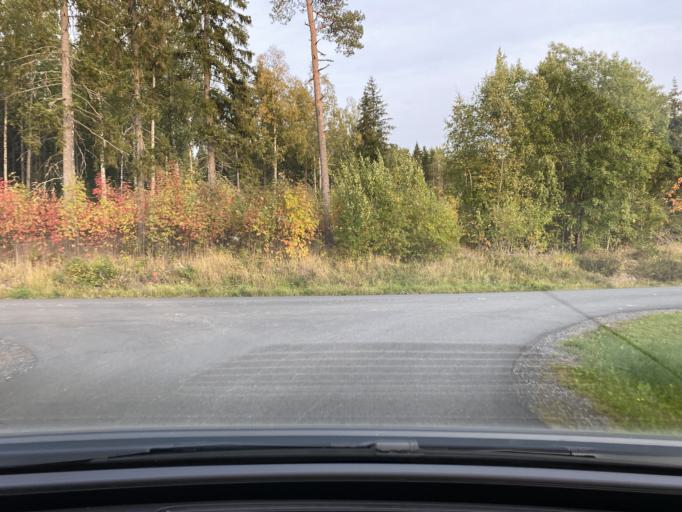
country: FI
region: Pirkanmaa
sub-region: Lounais-Pirkanmaa
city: Punkalaidun
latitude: 61.1221
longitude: 23.0849
